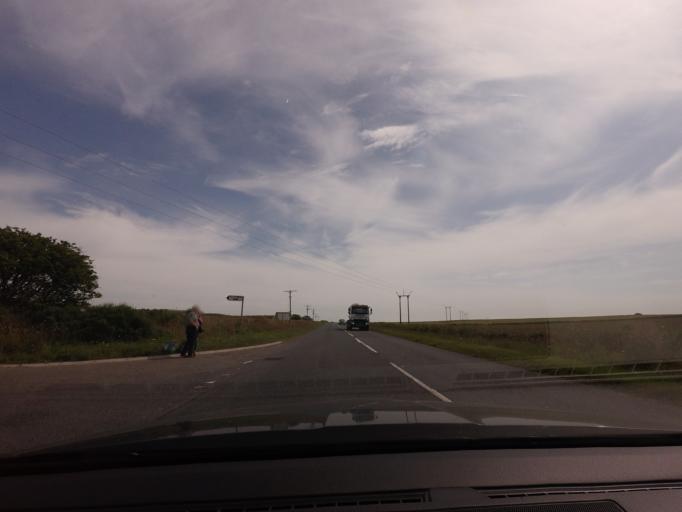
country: GB
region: Scotland
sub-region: Aberdeenshire
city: Peterhead
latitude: 57.5086
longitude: -1.8798
